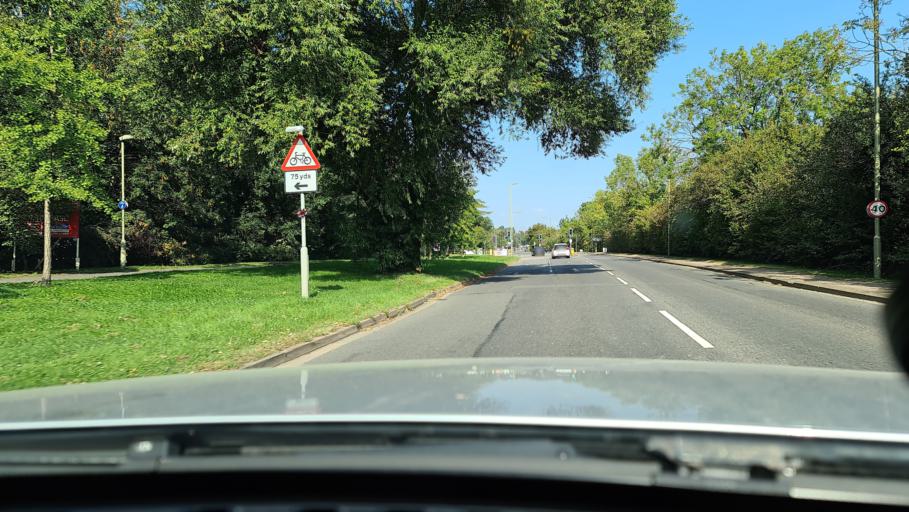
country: GB
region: England
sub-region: Oxfordshire
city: Banbury
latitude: 52.0749
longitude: -1.3368
